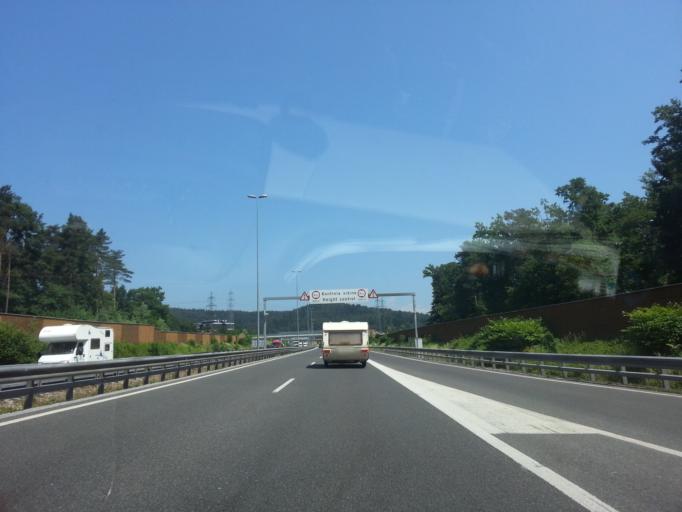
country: SI
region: Ljubljana
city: Ljubljana
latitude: 46.0765
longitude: 14.4601
